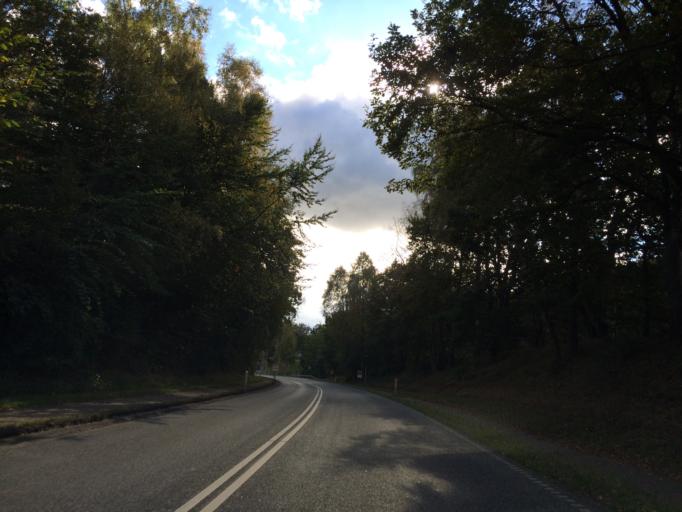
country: DK
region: Central Jutland
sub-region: Skanderborg Kommune
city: Ry
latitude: 56.1099
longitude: 9.7850
